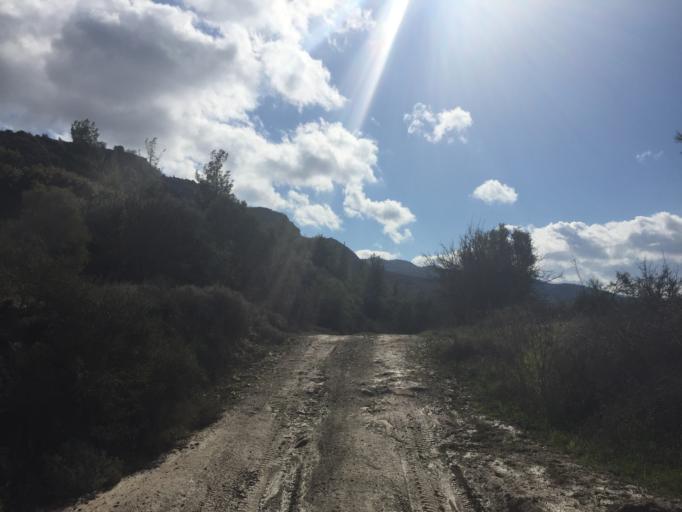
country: CY
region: Limassol
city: Pachna
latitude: 34.8852
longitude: 32.6774
